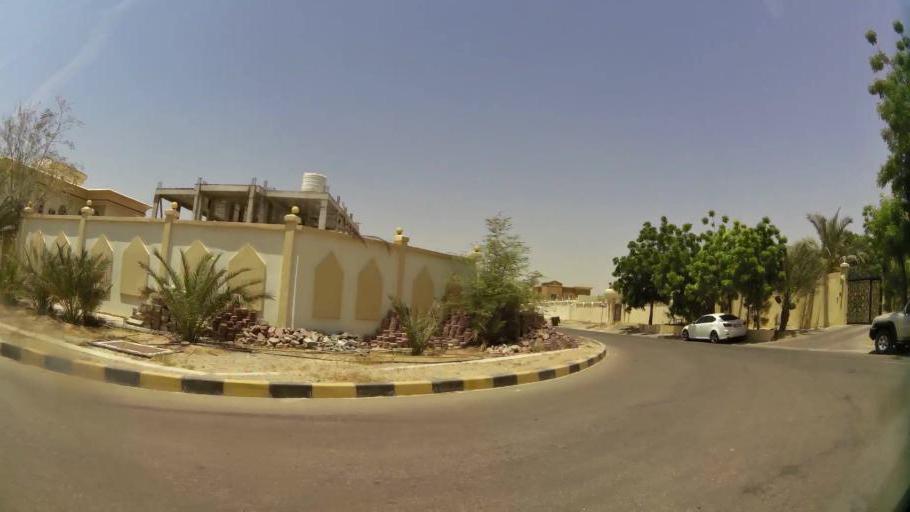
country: AE
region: Ajman
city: Ajman
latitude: 25.4183
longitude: 55.5110
